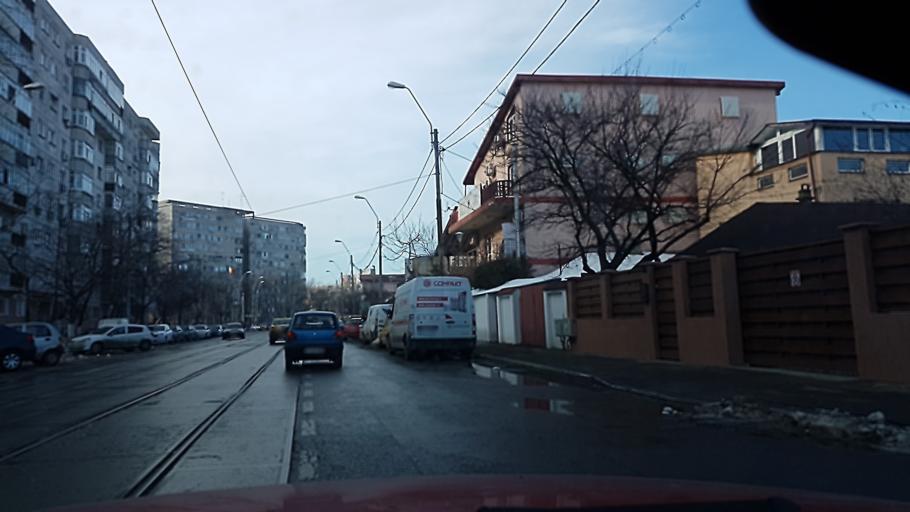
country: RO
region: Ilfov
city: Dobroesti
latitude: 44.4288
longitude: 26.1754
